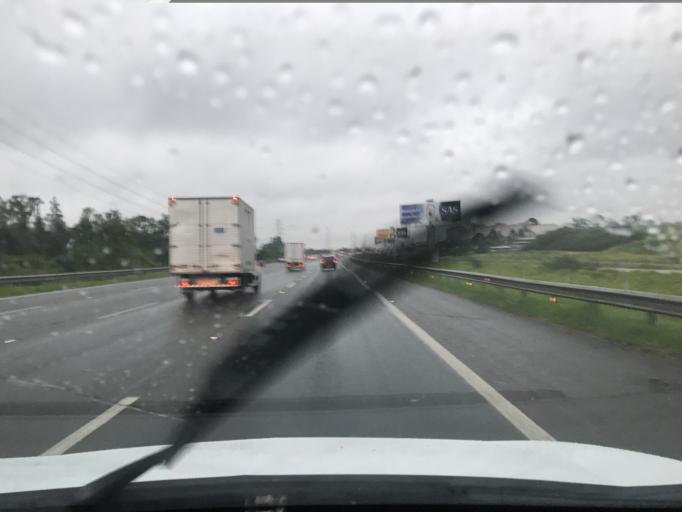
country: BR
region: Sao Paulo
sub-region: Guarulhos
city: Guarulhos
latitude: -23.4863
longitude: -46.5303
